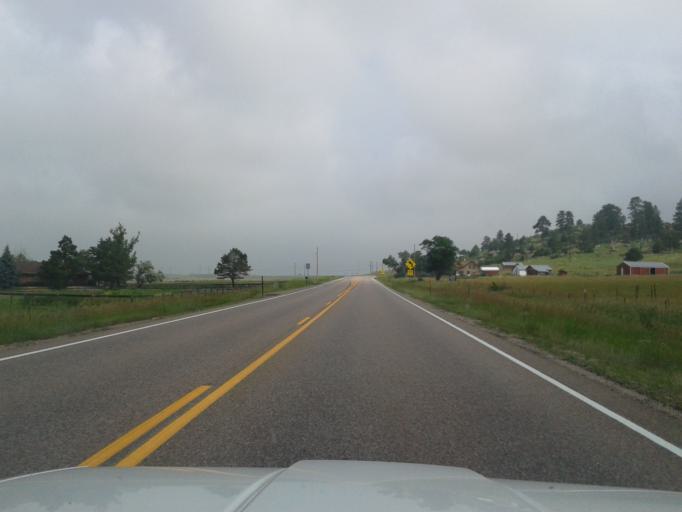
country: US
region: Colorado
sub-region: Elbert County
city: Elizabeth
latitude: 39.2566
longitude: -104.7019
